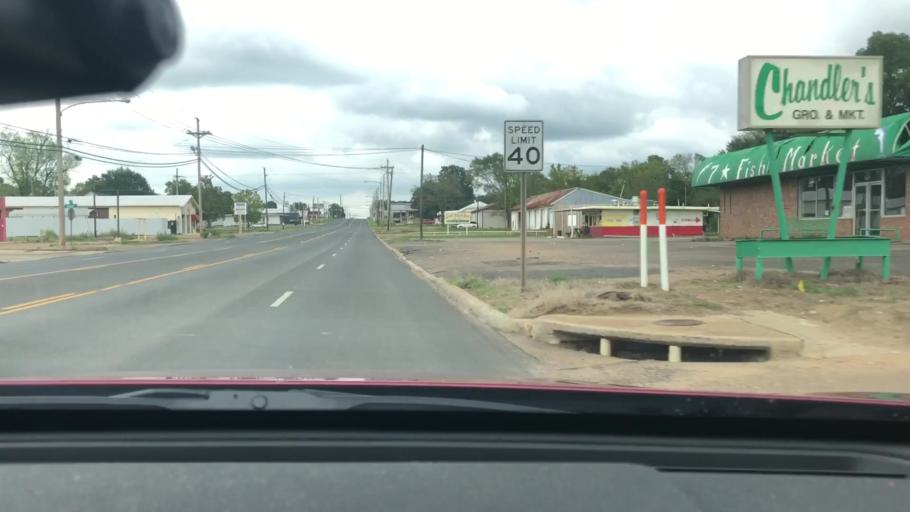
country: US
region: Arkansas
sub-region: Miller County
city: Texarkana
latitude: 33.4307
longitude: -94.0217
